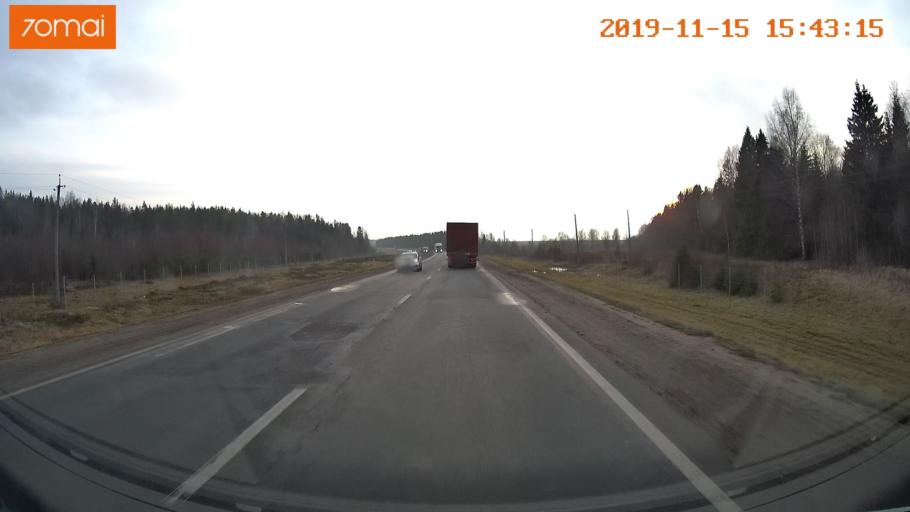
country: RU
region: Jaroslavl
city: Danilov
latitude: 57.9846
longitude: 40.0299
